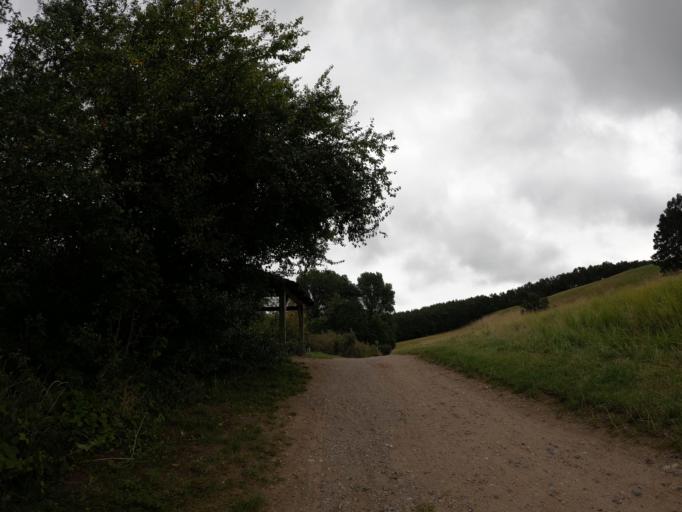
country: DE
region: Mecklenburg-Vorpommern
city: Ostseebad Gohren
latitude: 54.3055
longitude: 13.6954
